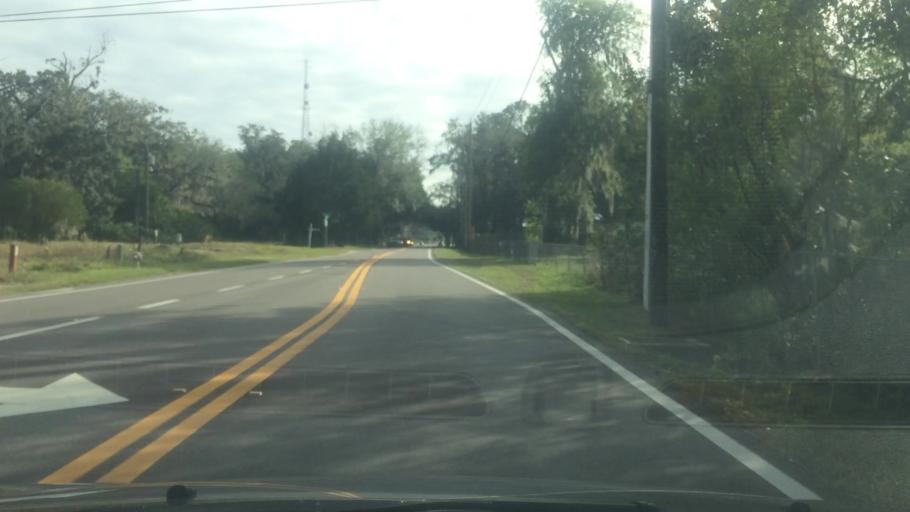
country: US
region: Florida
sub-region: Saint Johns County
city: Saint Augustine
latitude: 29.9195
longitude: -81.3609
